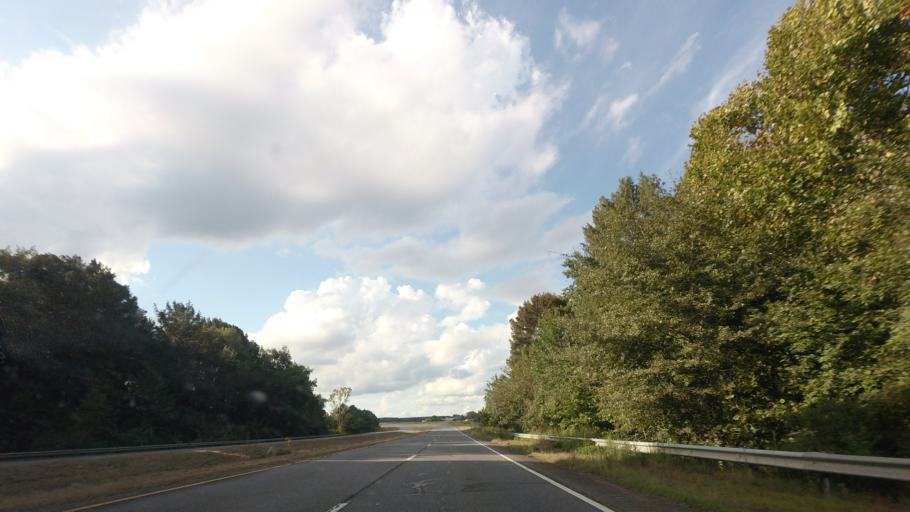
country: US
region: Georgia
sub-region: Houston County
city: Perry
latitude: 32.4072
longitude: -83.6468
